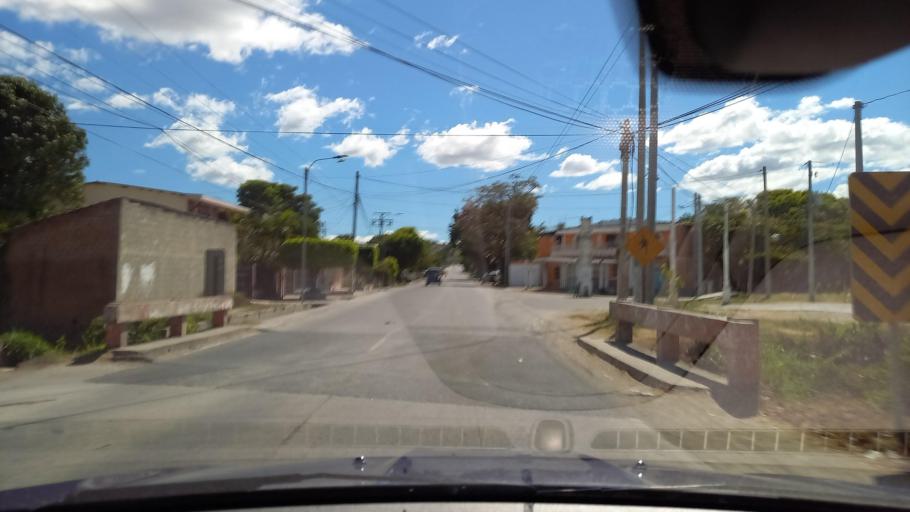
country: SV
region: Santa Ana
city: Metapan
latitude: 14.3379
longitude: -89.4483
